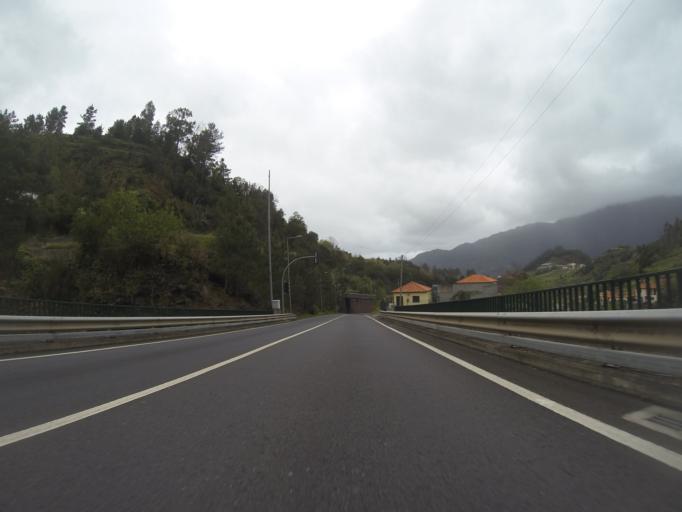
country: PT
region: Madeira
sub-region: Sao Vicente
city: Sao Vicente
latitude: 32.7699
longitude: -17.0307
